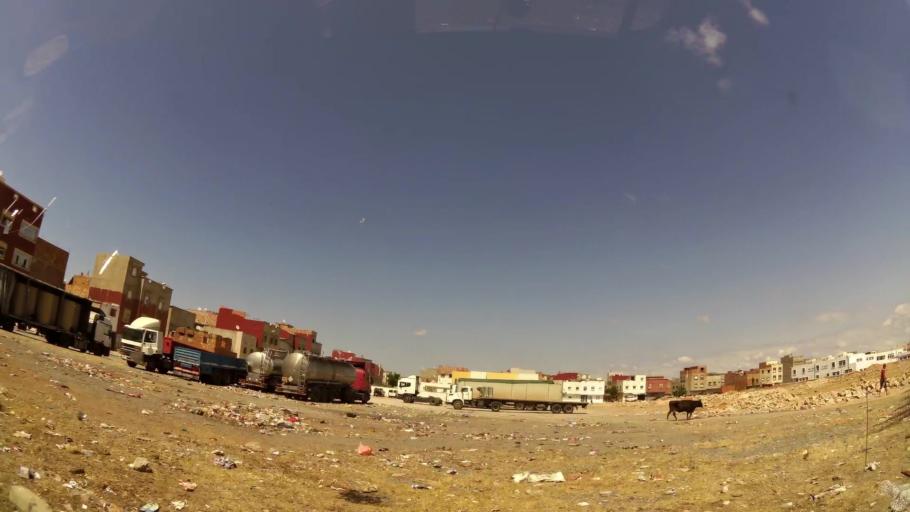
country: MA
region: Gharb-Chrarda-Beni Hssen
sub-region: Kenitra Province
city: Kenitra
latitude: 34.2282
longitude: -6.5496
